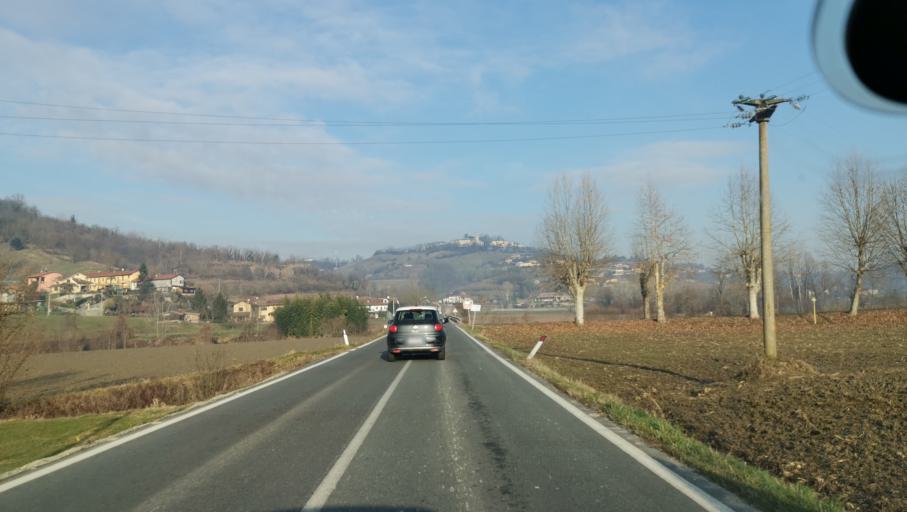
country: IT
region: Piedmont
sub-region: Provincia di Torino
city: Casalborgone
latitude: 45.1429
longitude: 7.9367
